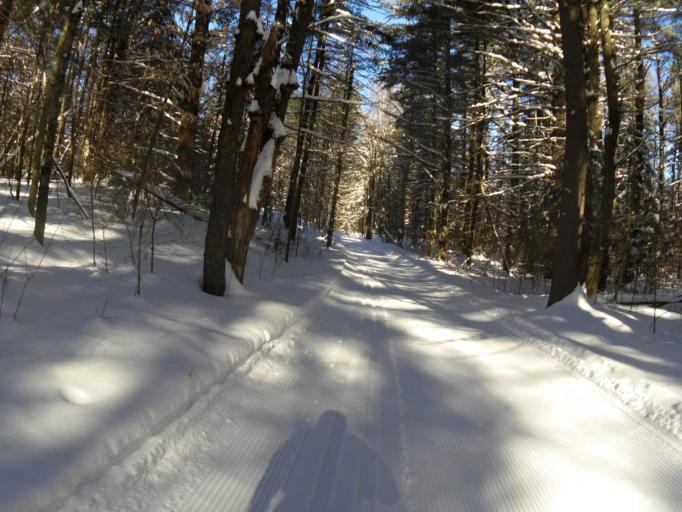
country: CA
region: Quebec
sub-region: Outaouais
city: Wakefield
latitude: 45.5922
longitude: -75.9693
